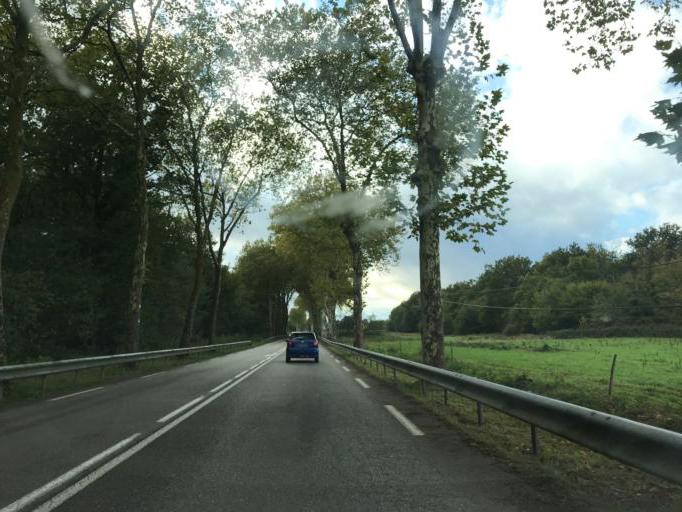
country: FR
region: Rhone-Alpes
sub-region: Departement de l'Ain
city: Saint-Andre-sur-Vieux-Jonc
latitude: 46.1758
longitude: 5.0633
